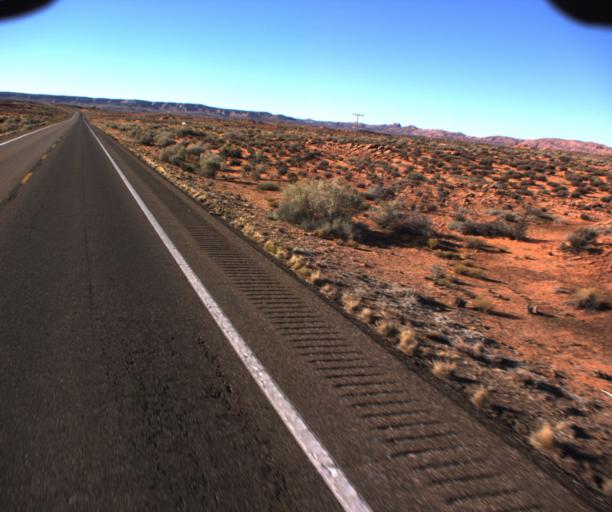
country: US
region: Arizona
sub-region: Coconino County
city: LeChee
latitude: 36.8591
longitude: -111.5057
